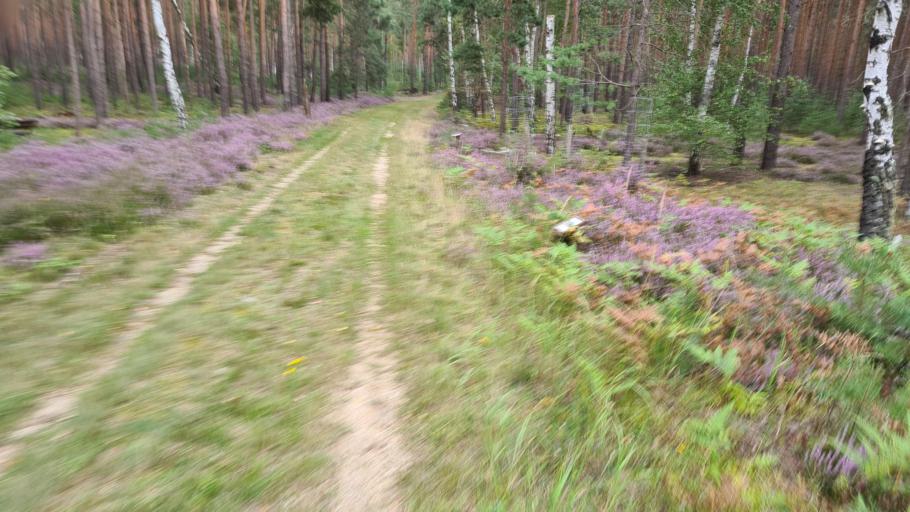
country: DE
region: Brandenburg
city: Schonborn
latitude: 51.6229
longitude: 13.4936
